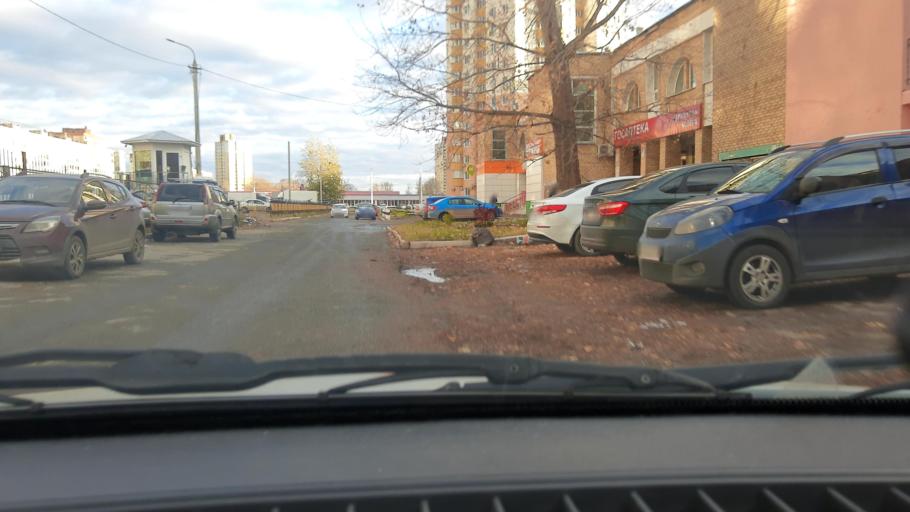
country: RU
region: Bashkortostan
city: Ufa
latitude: 54.7689
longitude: 56.0695
